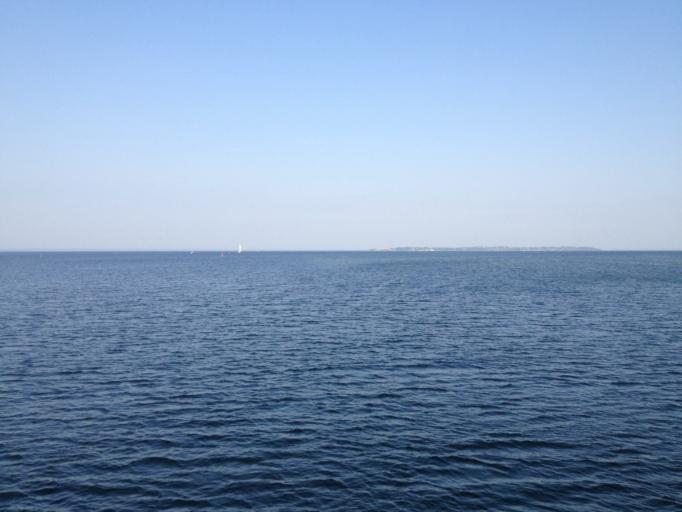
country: SE
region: Skane
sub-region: Landskrona
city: Landskrona
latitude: 55.8673
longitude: 12.8157
